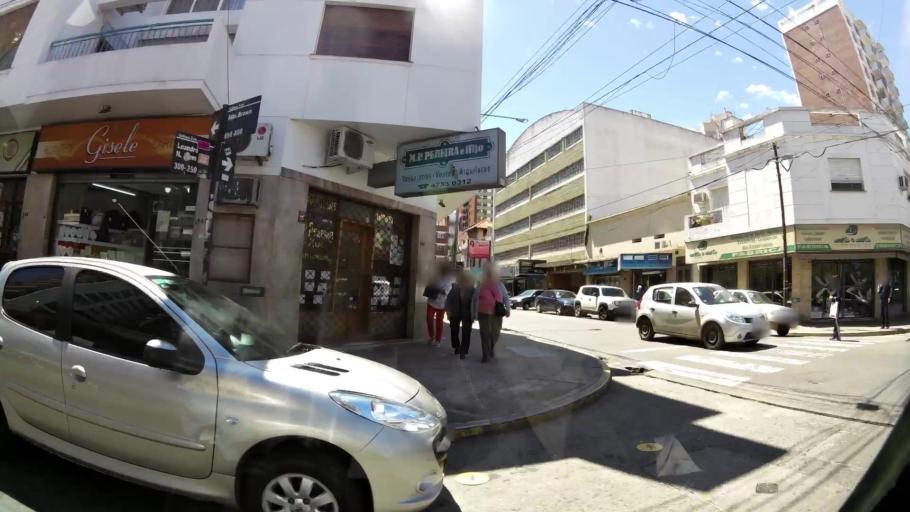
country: AR
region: Buenos Aires
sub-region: Partido de Quilmes
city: Quilmes
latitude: -34.7223
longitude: -58.2559
